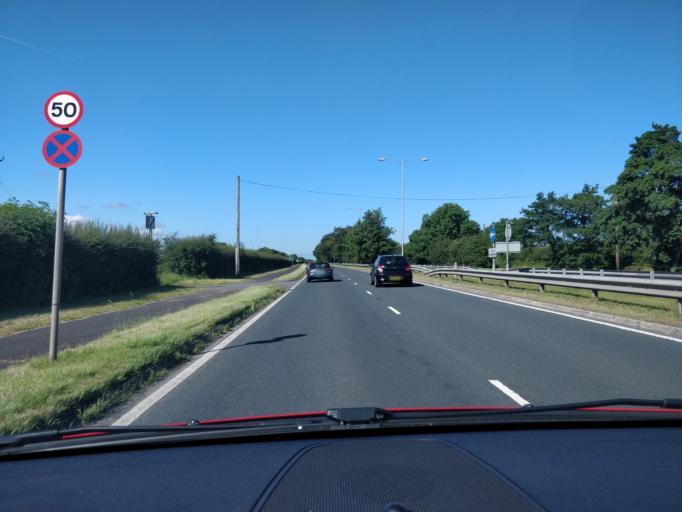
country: GB
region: England
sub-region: Lancashire
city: Tarleton
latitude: 53.6670
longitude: -2.8628
